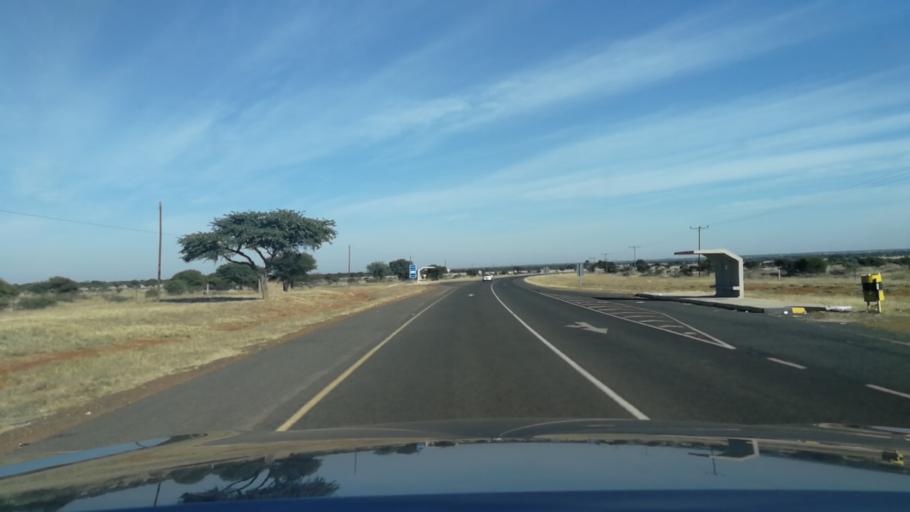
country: BW
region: South East
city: Janeng
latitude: -25.4787
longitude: 25.5085
